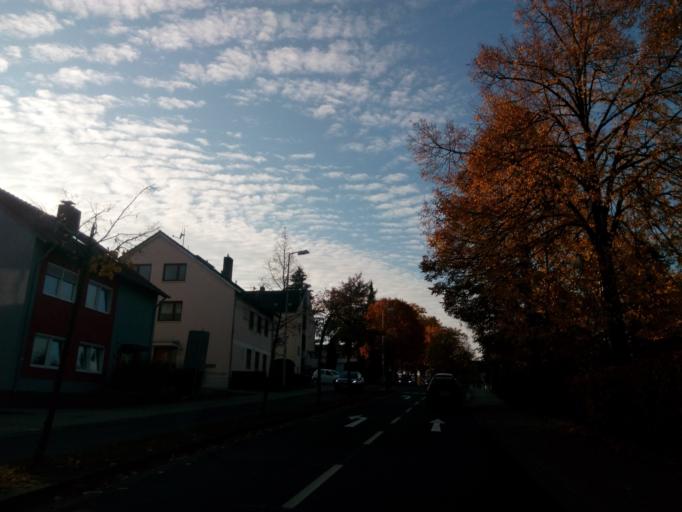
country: DE
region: Saarland
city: Sulzbach
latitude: 49.2741
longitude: 7.0398
